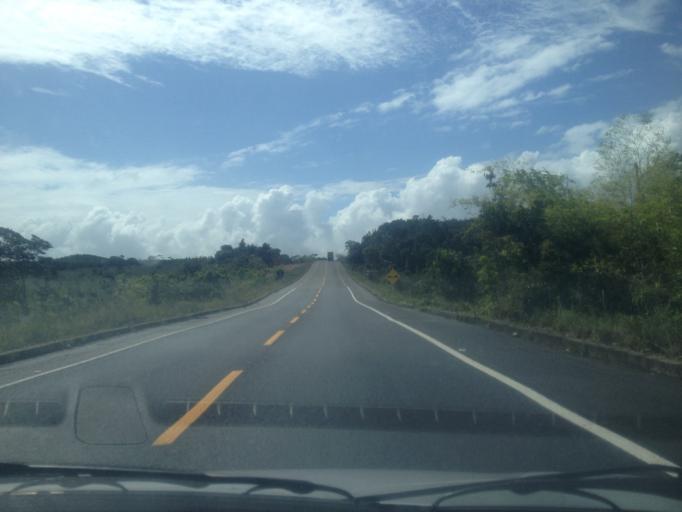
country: BR
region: Bahia
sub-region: Conde
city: Conde
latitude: -11.6750
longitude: -37.5624
